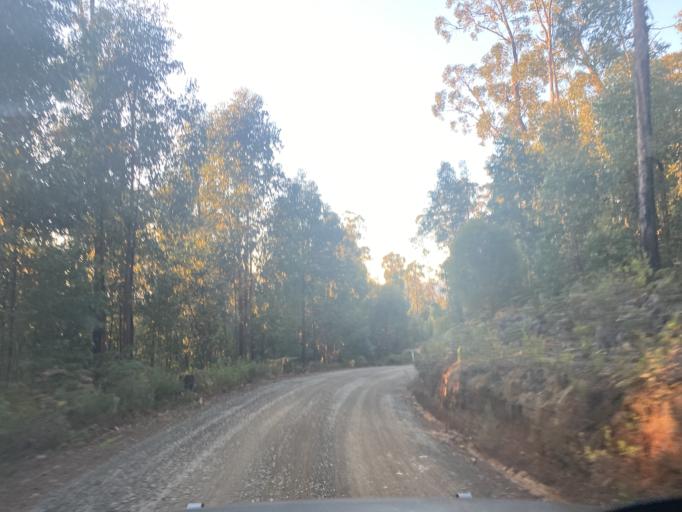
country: AU
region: Victoria
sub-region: Yarra Ranges
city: Healesville
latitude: -37.4210
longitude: 145.5293
